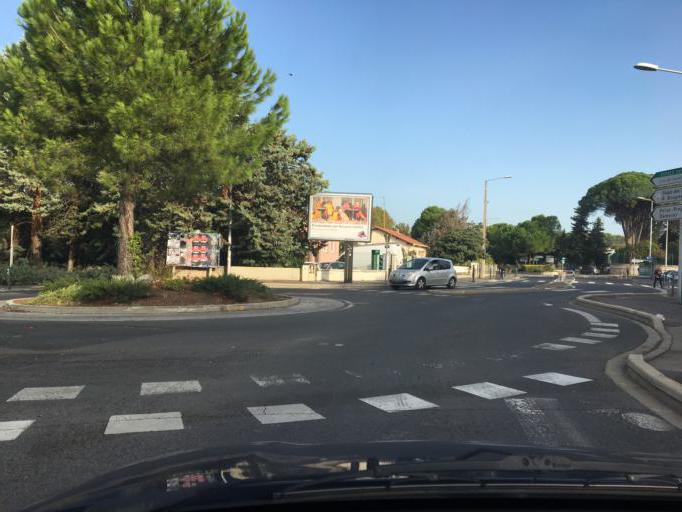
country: FR
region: Languedoc-Roussillon
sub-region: Departement de l'Herault
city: Montpellier
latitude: 43.6346
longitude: 3.8682
